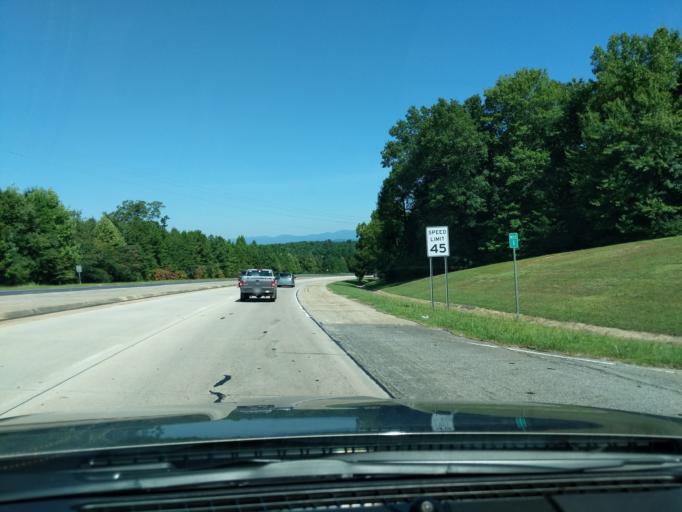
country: US
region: Georgia
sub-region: Habersham County
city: Baldwin
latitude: 34.5016
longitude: -83.5444
